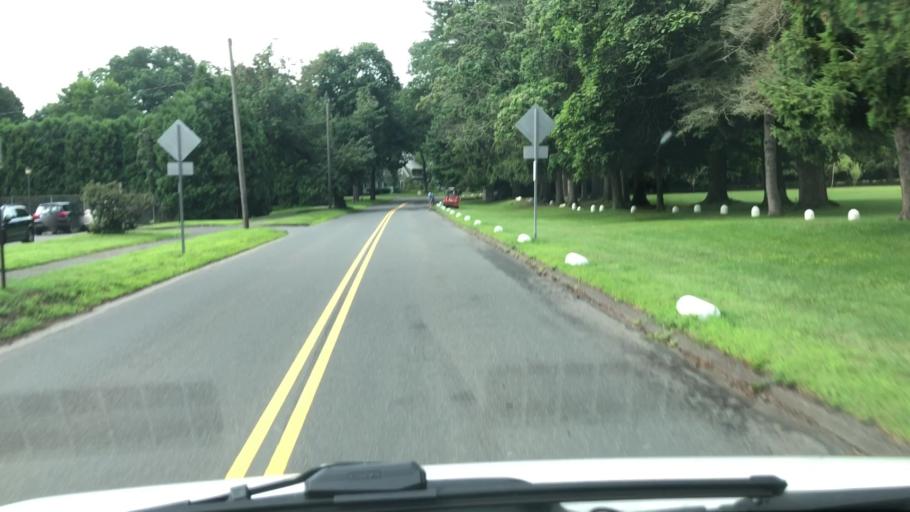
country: US
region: Massachusetts
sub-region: Hampshire County
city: Northampton
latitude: 42.3292
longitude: -72.6453
